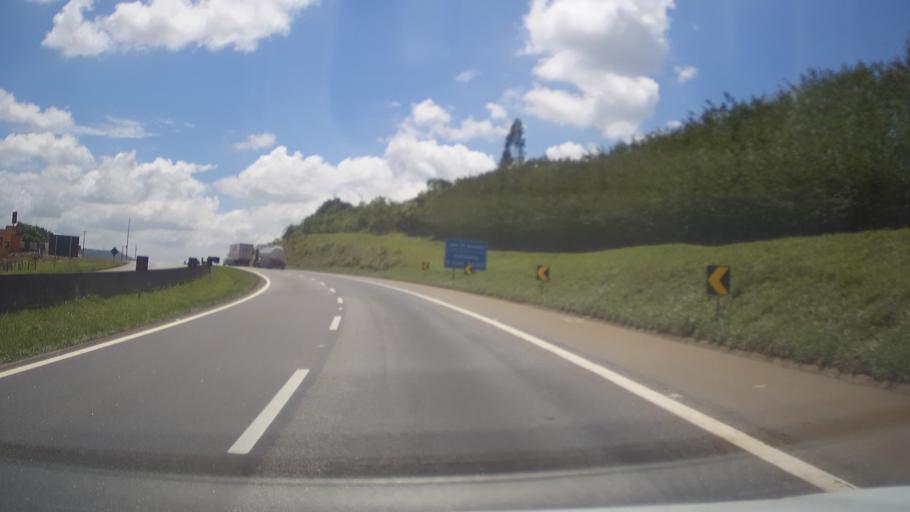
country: BR
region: Minas Gerais
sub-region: Campanha
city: Campanha
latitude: -21.8356
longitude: -45.5046
